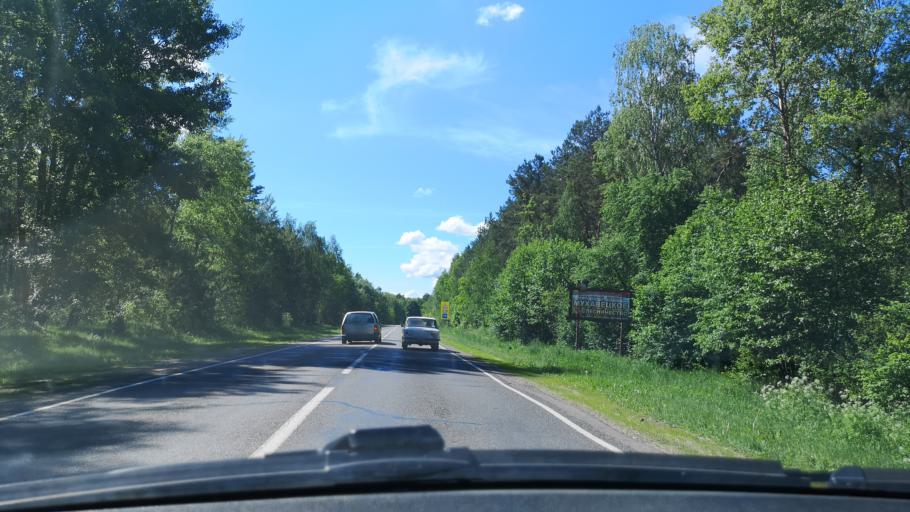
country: BY
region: Brest
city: Brest
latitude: 52.0258
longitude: 23.7299
